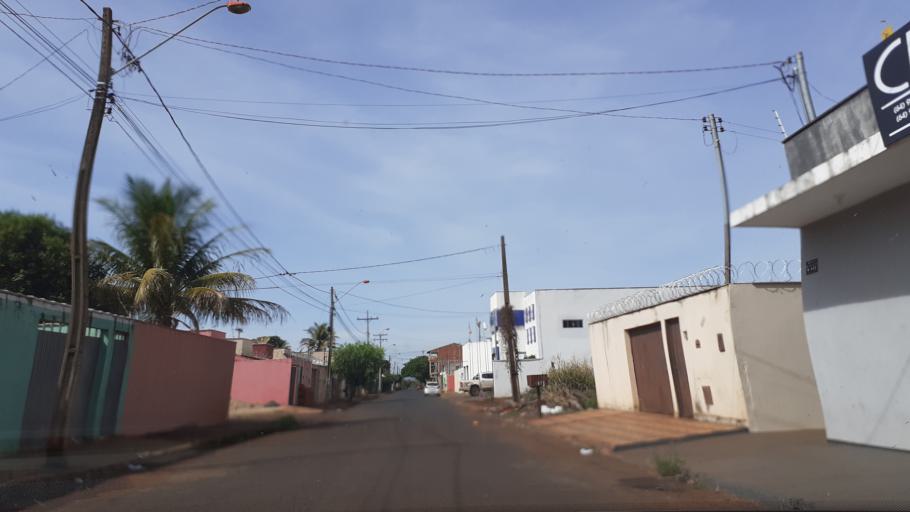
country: BR
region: Goias
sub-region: Itumbiara
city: Itumbiara
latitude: -18.4140
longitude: -49.2541
